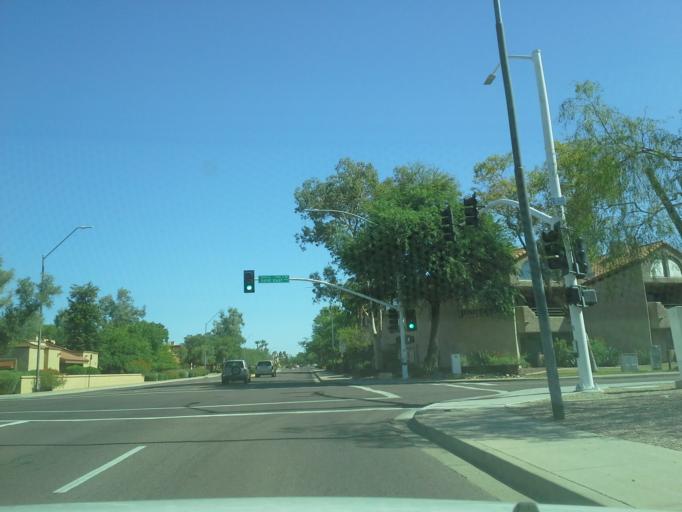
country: US
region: Arizona
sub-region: Maricopa County
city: Paradise Valley
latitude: 33.5782
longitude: -111.9303
